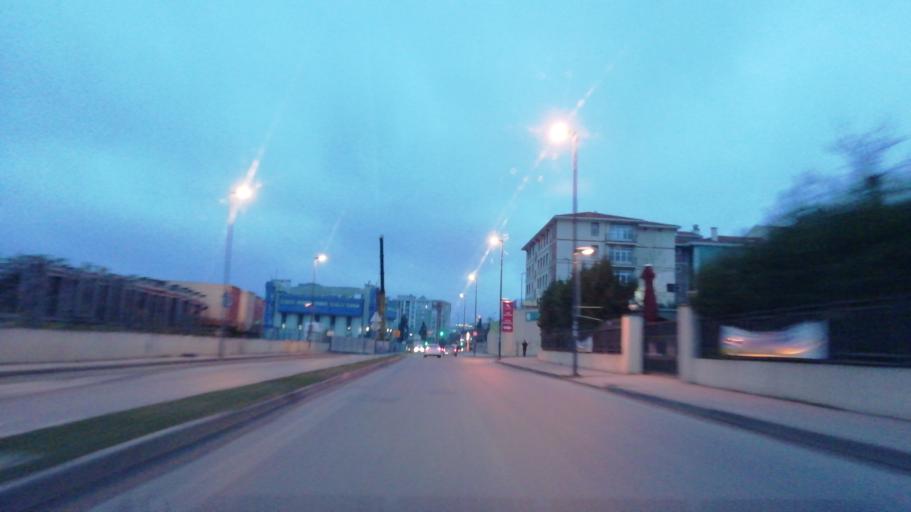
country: TR
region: Istanbul
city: Mahmutbey
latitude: 41.0136
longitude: 28.8182
